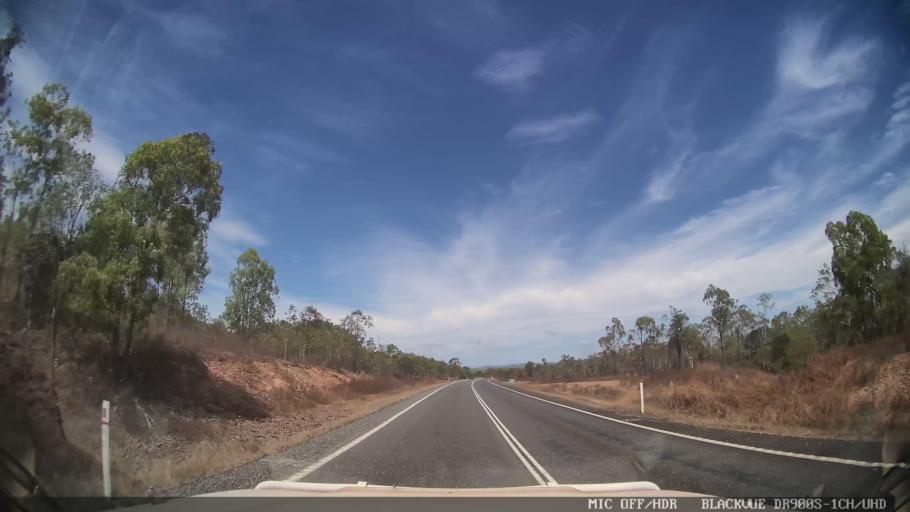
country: AU
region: Queensland
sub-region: Cook
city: Cooktown
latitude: -15.7060
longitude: 145.0258
